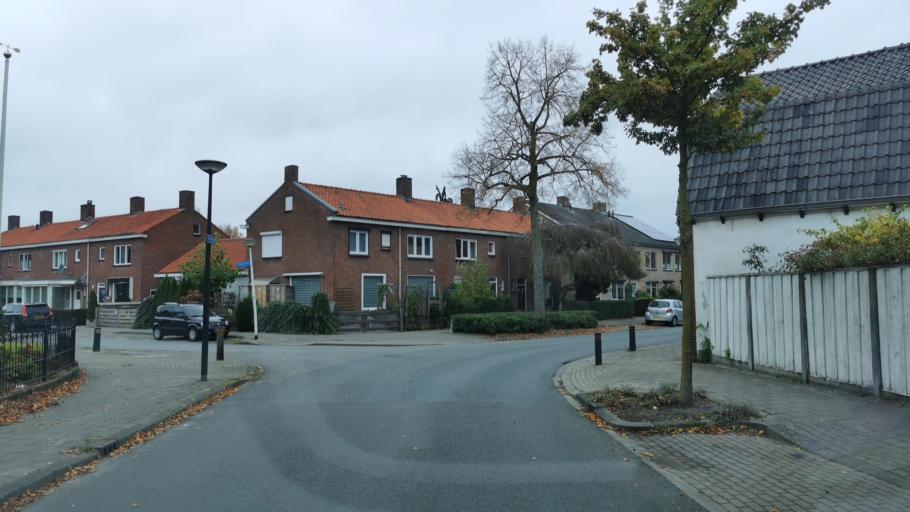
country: DE
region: North Rhine-Westphalia
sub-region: Regierungsbezirk Munster
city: Gronau
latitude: 52.2132
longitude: 6.9746
